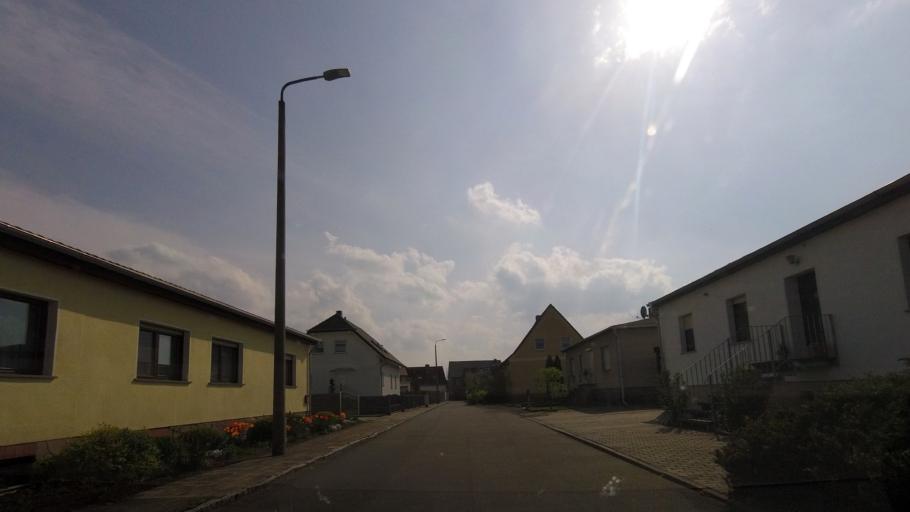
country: DE
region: Saxony-Anhalt
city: Seyda
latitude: 51.9570
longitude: 12.8925
